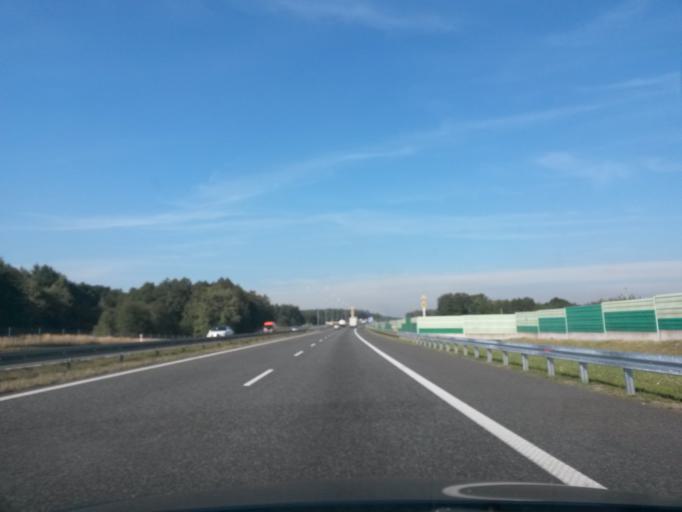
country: PL
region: Silesian Voivodeship
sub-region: Powiat gliwicki
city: Sosnicowice
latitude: 50.3035
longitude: 18.5538
